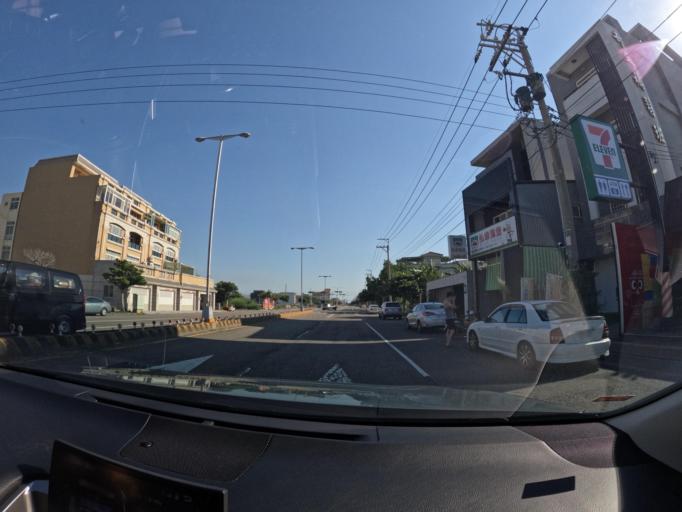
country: TW
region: Taiwan
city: Fengyuan
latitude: 24.2604
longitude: 120.5540
